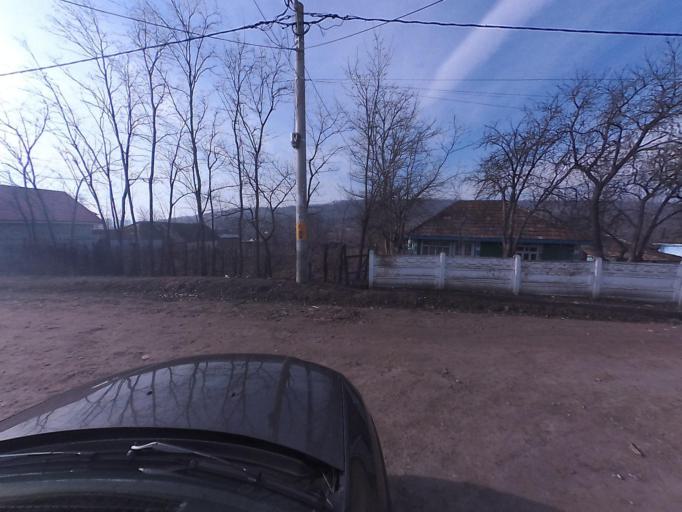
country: RO
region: Vaslui
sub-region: Comuna Solesti
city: Solesti
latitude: 46.8069
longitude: 27.7830
